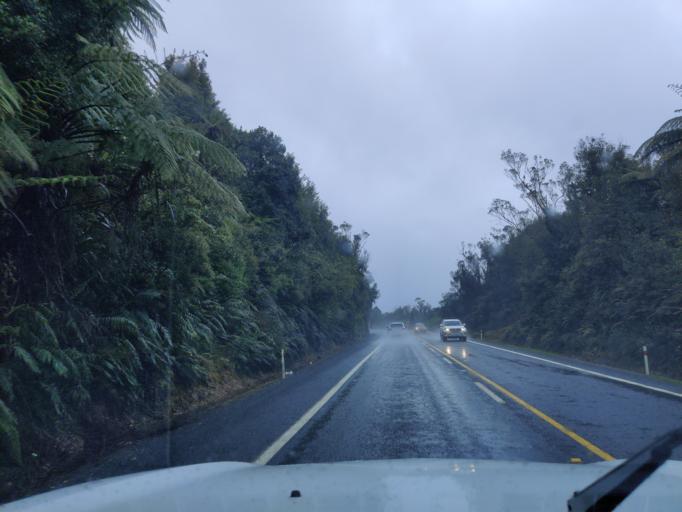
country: NZ
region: Waikato
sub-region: South Waikato District
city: Tokoroa
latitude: -38.0287
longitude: 175.9703
